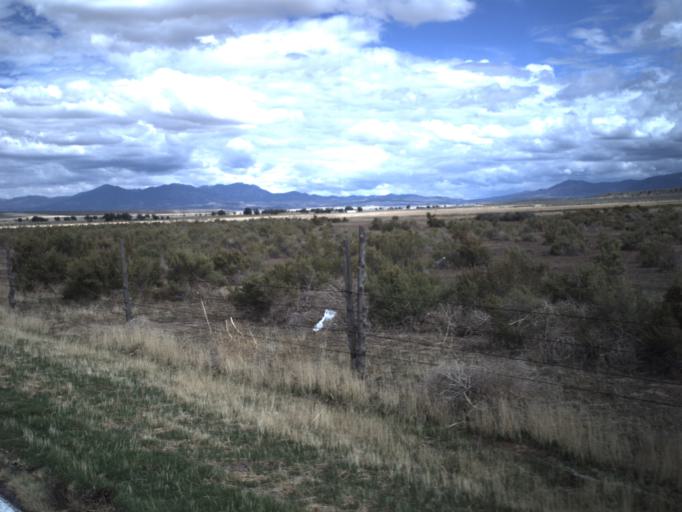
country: US
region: Utah
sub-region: Millard County
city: Fillmore
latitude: 39.0168
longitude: -112.4100
